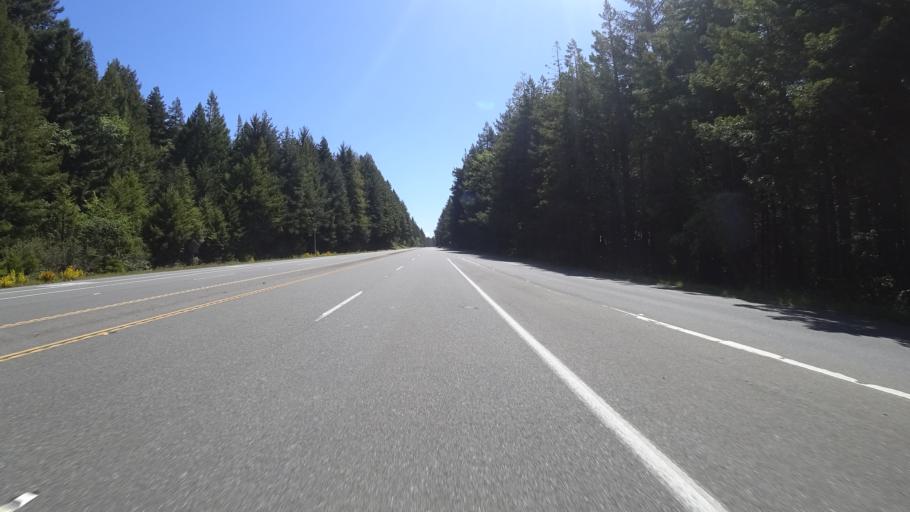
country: US
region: California
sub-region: Humboldt County
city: Westhaven-Moonstone
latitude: 41.0616
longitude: -124.1384
